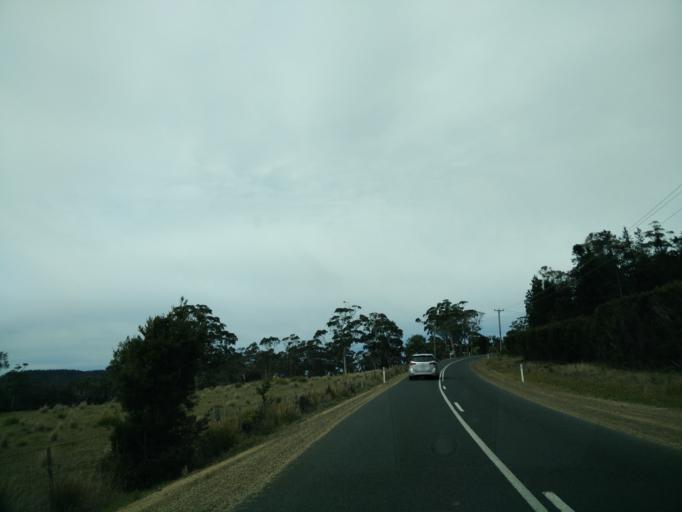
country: AU
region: Tasmania
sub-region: Break O'Day
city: St Helens
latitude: -41.9155
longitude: 148.2483
